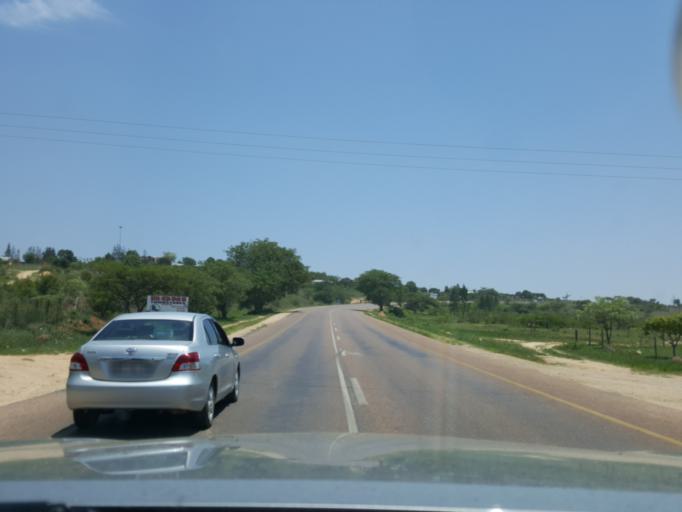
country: ZA
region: Limpopo
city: Thulamahashi
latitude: -24.7074
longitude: 31.0271
